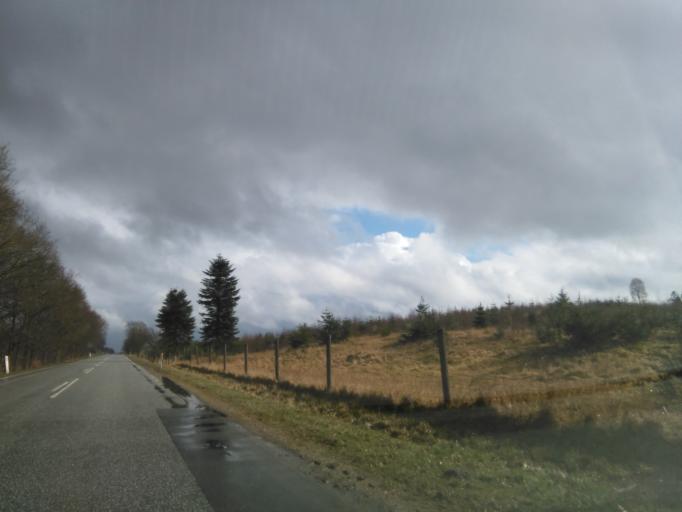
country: DK
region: Central Jutland
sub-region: Silkeborg Kommune
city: Svejbaek
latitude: 56.0896
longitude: 9.6778
